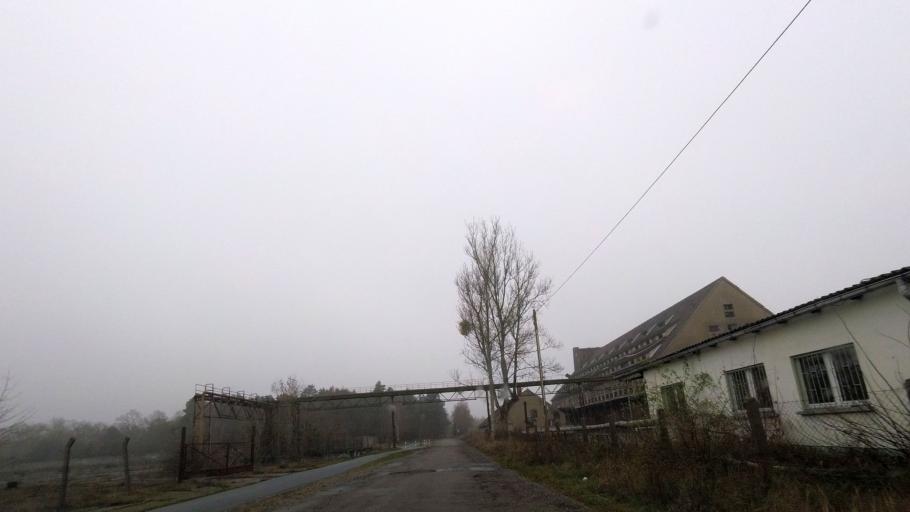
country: DE
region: Brandenburg
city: Juterbog
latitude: 51.9983
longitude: 13.0312
